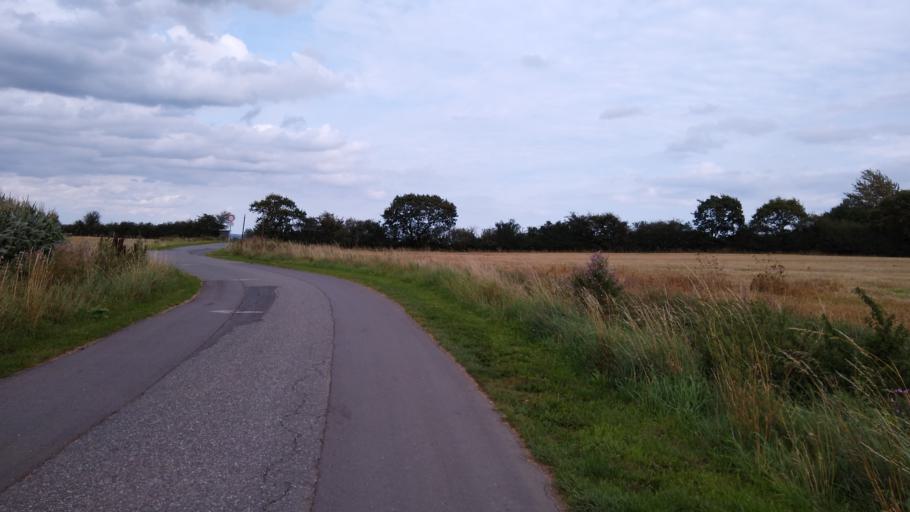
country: DK
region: South Denmark
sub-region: Fredericia Kommune
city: Fredericia
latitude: 55.6081
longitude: 9.7815
